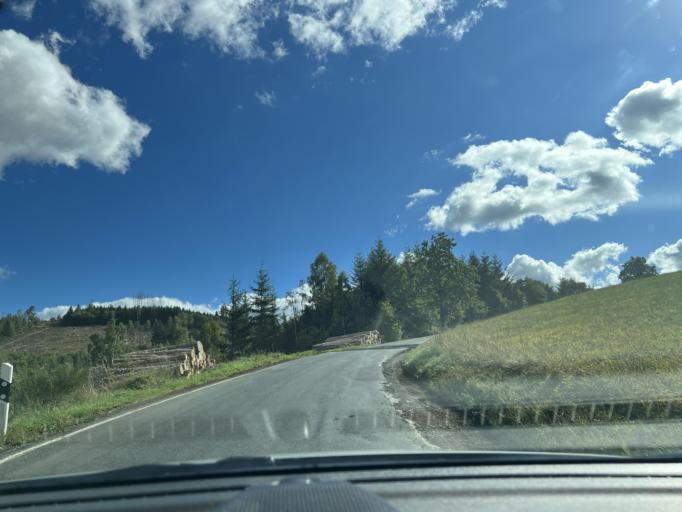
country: DE
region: North Rhine-Westphalia
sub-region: Regierungsbezirk Arnsberg
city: Erndtebruck
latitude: 50.9996
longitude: 8.3370
